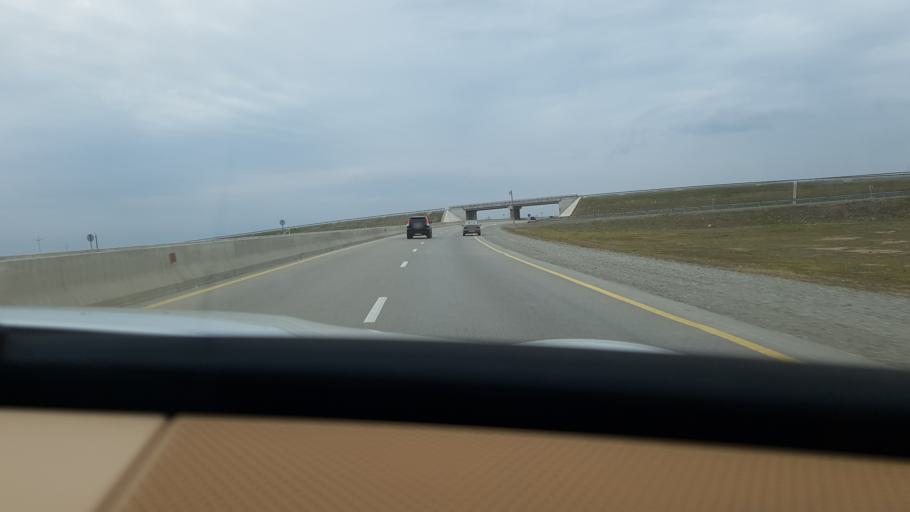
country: AZ
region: Haciqabul
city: Haciqabul
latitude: 40.0077
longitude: 48.9103
